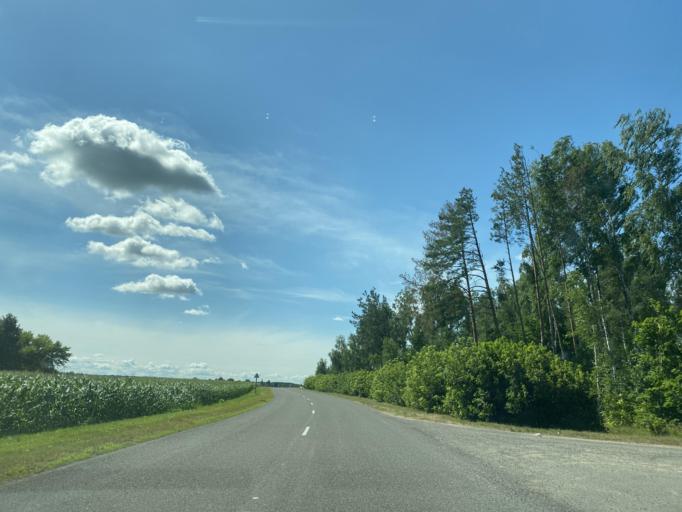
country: BY
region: Brest
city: Ivanava
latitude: 52.2196
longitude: 25.6305
